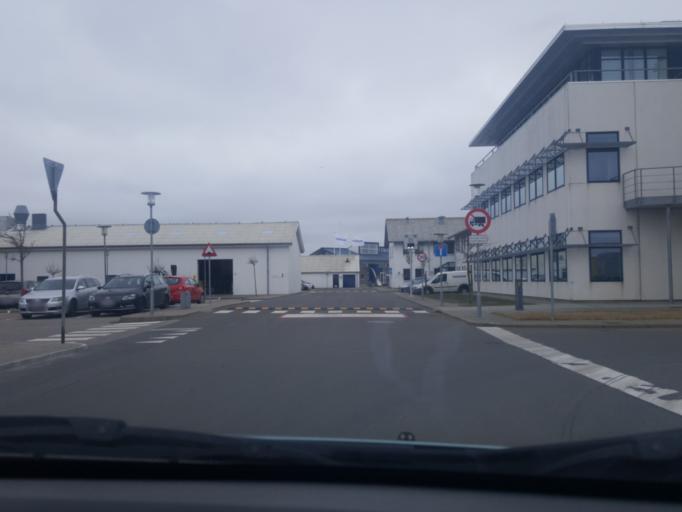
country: DK
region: Central Jutland
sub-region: Ringkobing-Skjern Kommune
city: Ringkobing
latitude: 56.0888
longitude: 8.2376
